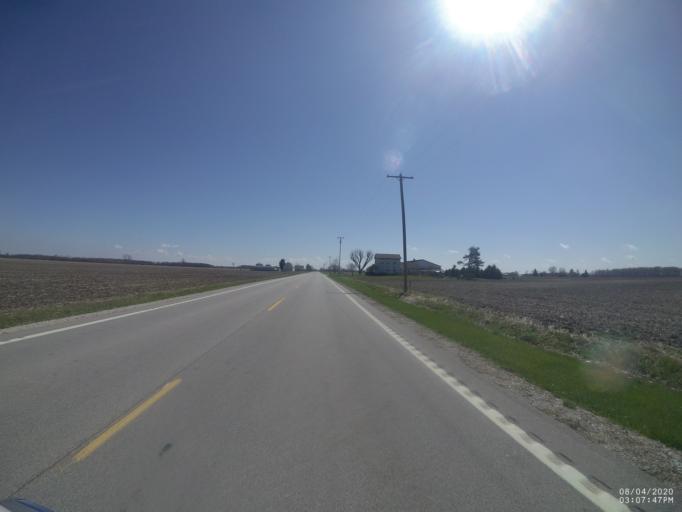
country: US
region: Ohio
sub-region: Sandusky County
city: Stony Prairie
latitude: 41.2926
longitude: -83.2358
